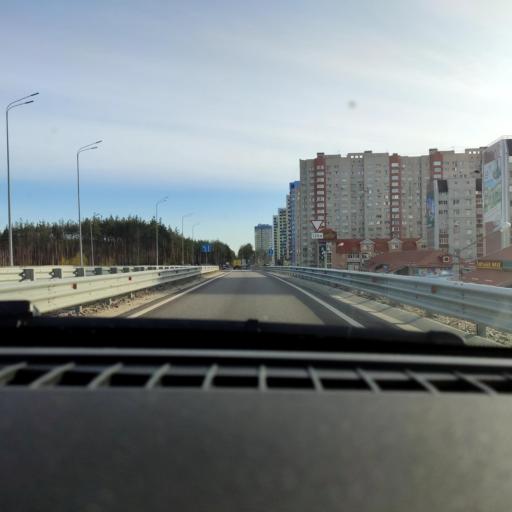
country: RU
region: Voronezj
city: Somovo
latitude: 51.7418
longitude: 39.3105
